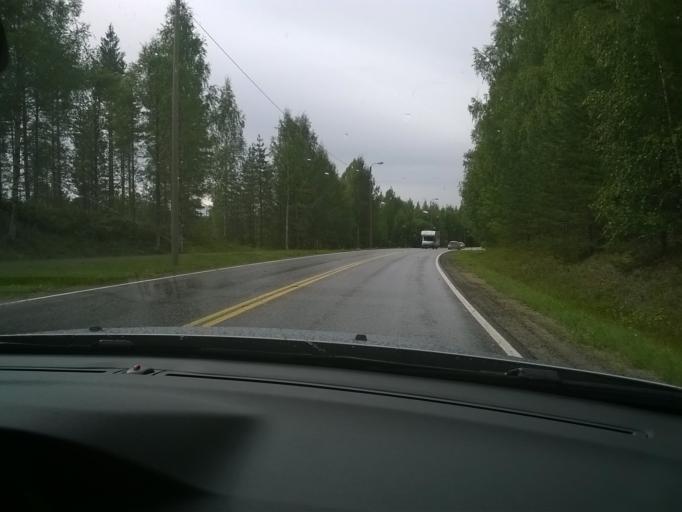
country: FI
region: Kainuu
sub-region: Kehys-Kainuu
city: Kuhmo
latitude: 64.1190
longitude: 29.5754
